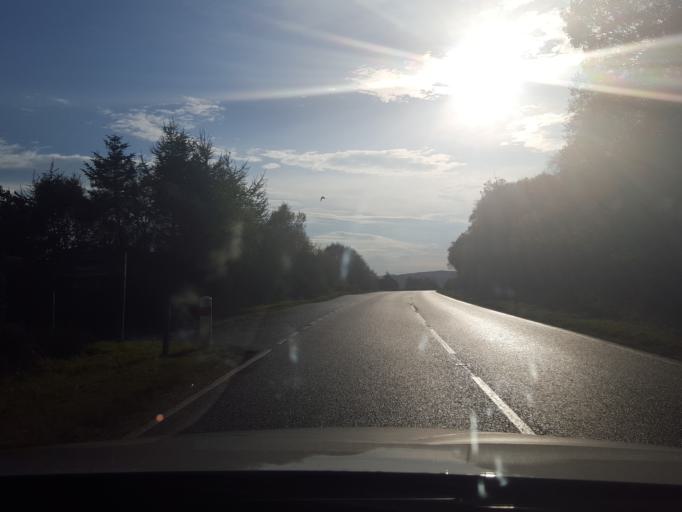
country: GB
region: Scotland
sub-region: Highland
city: Portree
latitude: 57.2580
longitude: -5.9414
